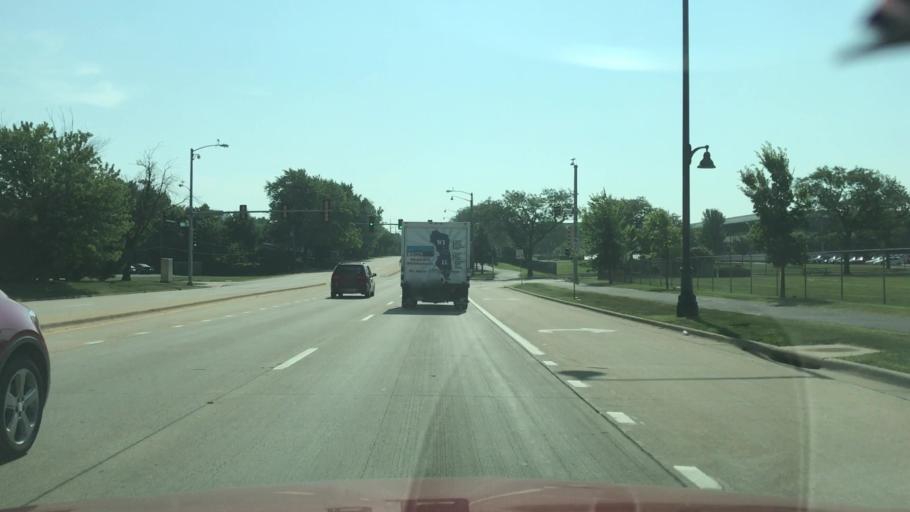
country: US
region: Illinois
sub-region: Winnebago County
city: Rockford
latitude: 42.2382
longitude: -89.0277
